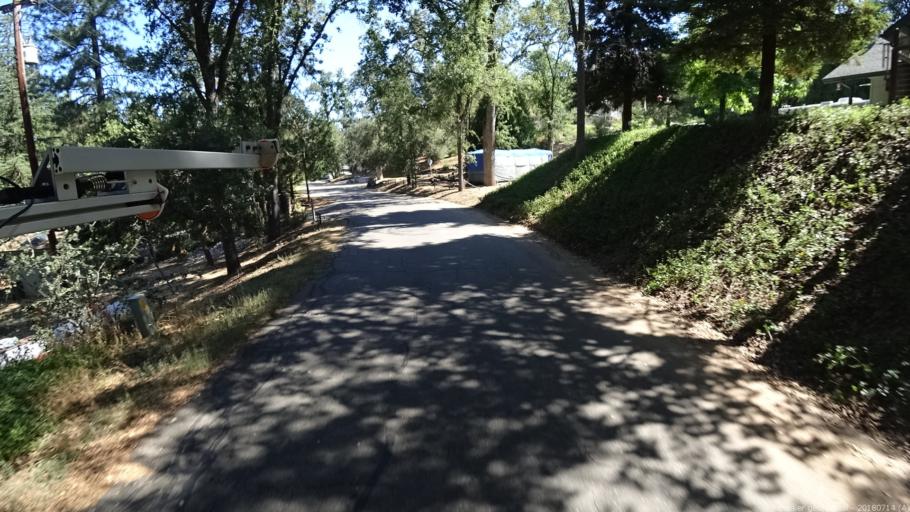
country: US
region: California
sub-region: Madera County
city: Oakhurst
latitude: 37.3687
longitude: -119.6264
